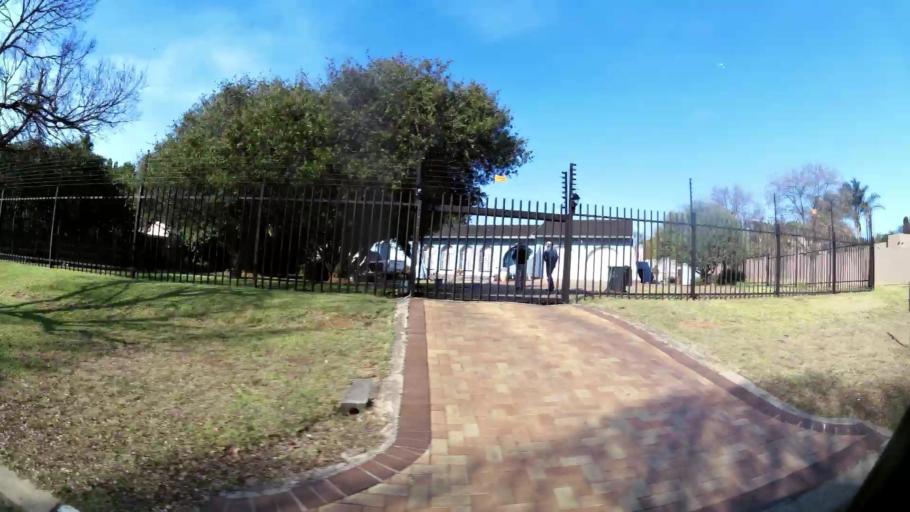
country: ZA
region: Gauteng
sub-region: City of Johannesburg Metropolitan Municipality
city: Roodepoort
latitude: -26.0977
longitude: 27.9737
